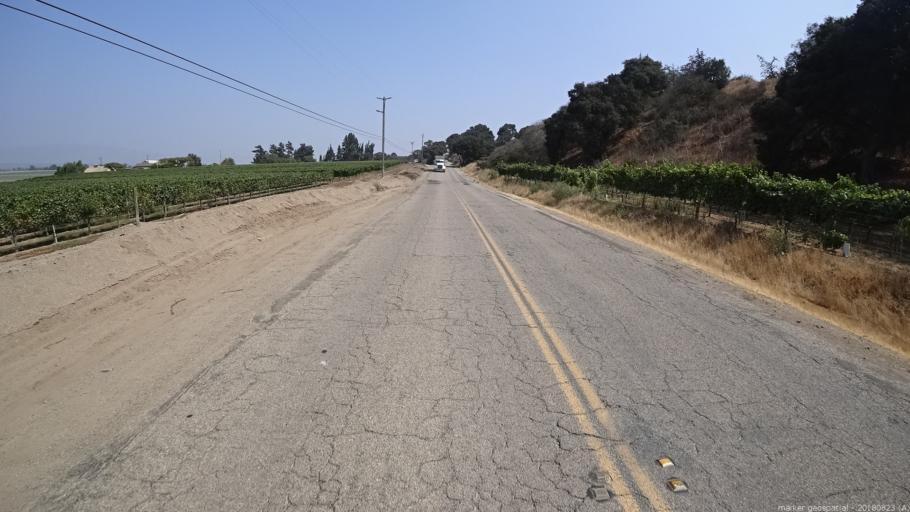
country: US
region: California
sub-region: Monterey County
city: Gonzales
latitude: 36.4721
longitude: -121.4698
